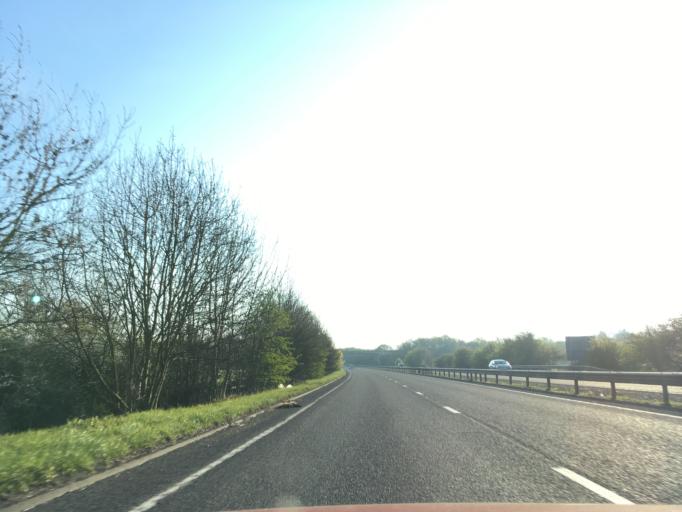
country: GB
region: England
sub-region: Oxfordshire
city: Ducklington
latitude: 51.7763
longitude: -1.4734
